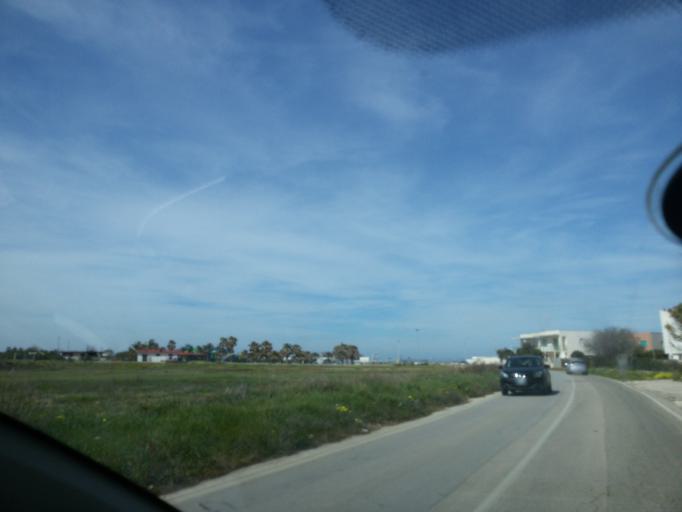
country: IT
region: Apulia
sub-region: Provincia di Brindisi
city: Pezze di Greco
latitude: 40.8420
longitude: 17.4648
